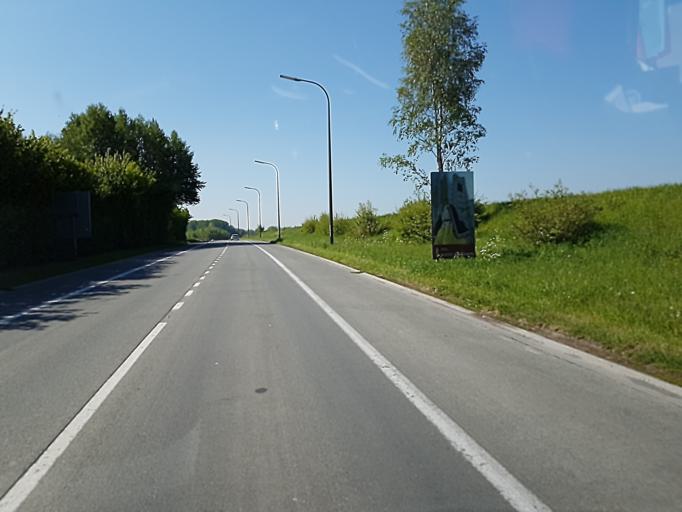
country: BE
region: Wallonia
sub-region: Province du Hainaut
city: Ath
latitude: 50.6753
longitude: 3.7991
